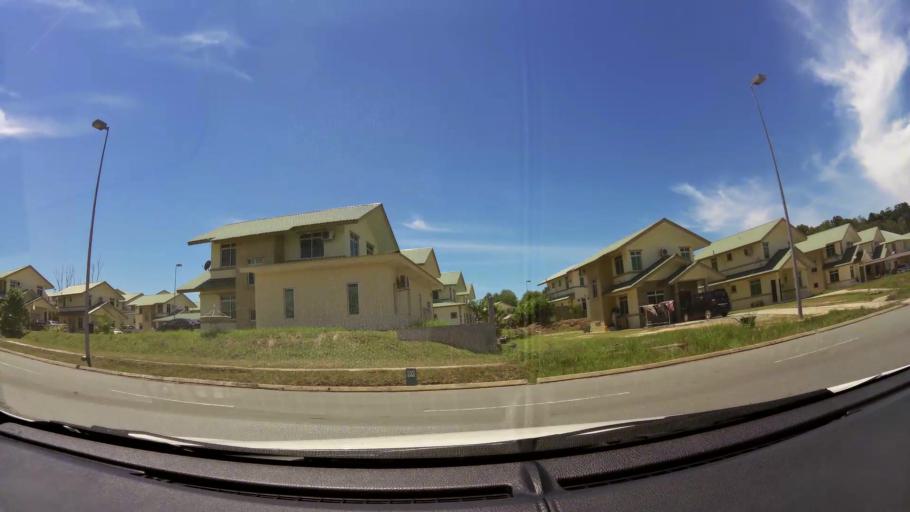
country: BN
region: Brunei and Muara
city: Bandar Seri Begawan
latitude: 5.0276
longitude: 115.0331
